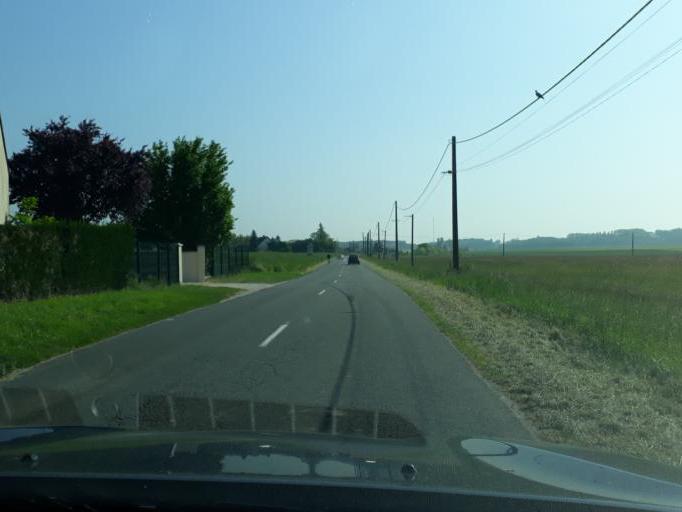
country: FR
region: Centre
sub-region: Departement du Loiret
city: Vennecy
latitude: 47.9462
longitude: 2.0636
